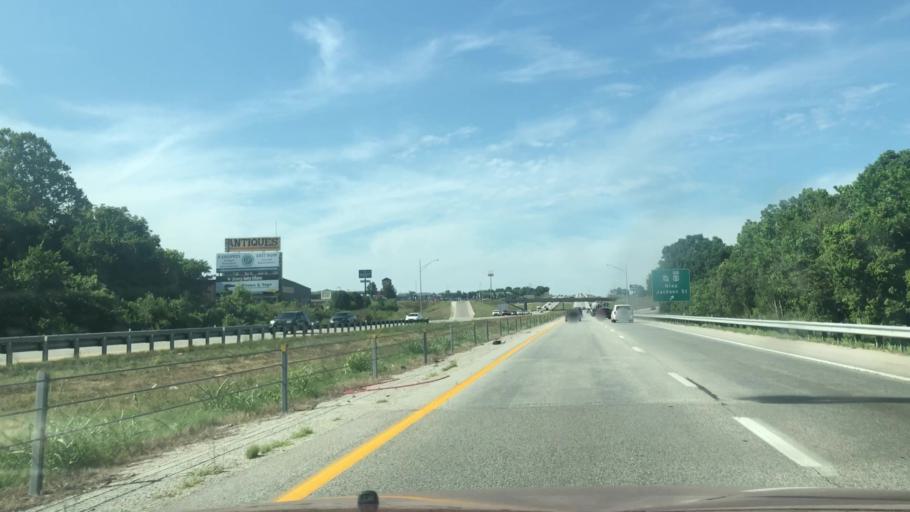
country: US
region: Missouri
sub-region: Christian County
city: Ozark
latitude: 37.0180
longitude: -93.2289
